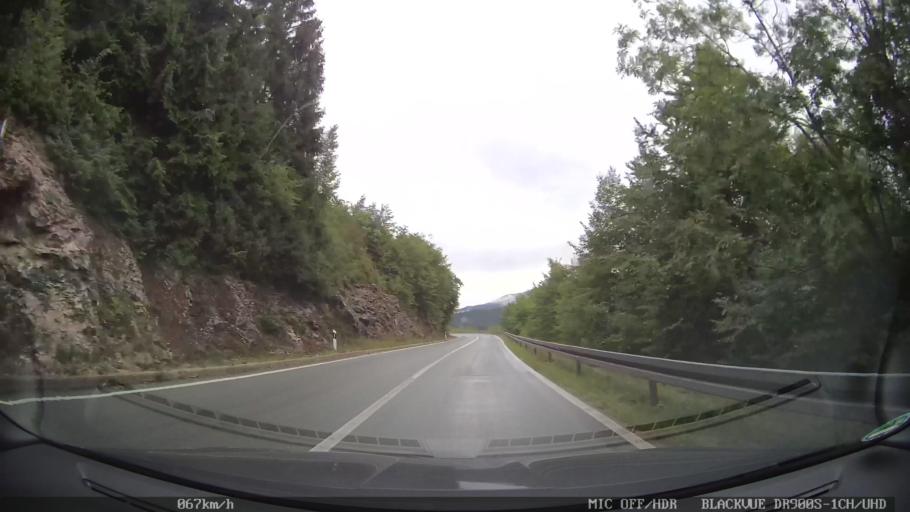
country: HR
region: Licko-Senjska
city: Jezerce
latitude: 44.7722
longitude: 15.6574
